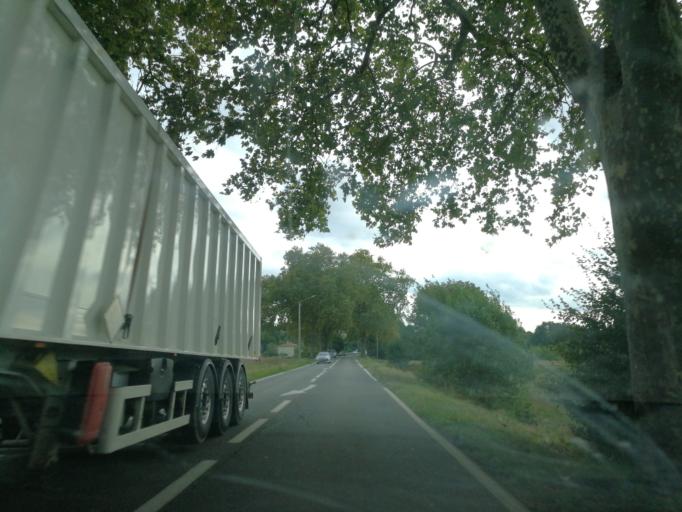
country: FR
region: Midi-Pyrenees
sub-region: Departement de la Haute-Garonne
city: Dremil-Lafage
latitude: 43.5909
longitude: 1.5870
